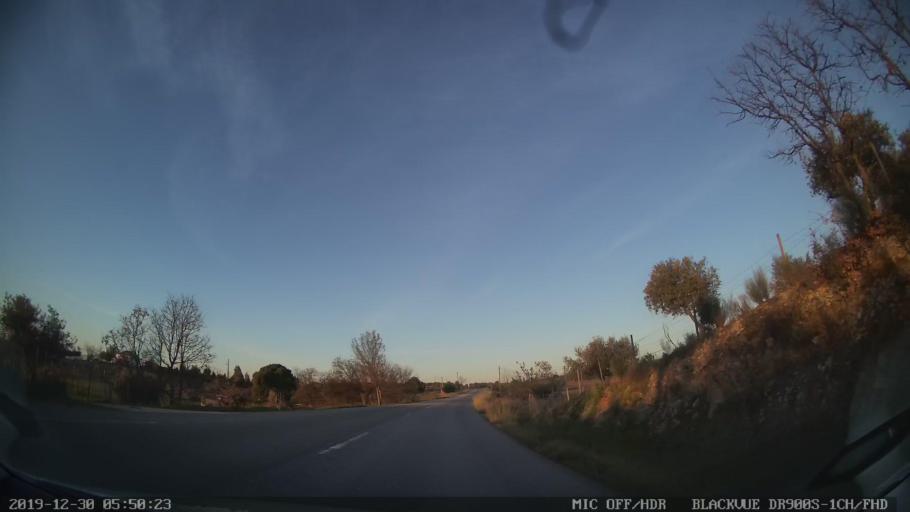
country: PT
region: Castelo Branco
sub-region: Idanha-A-Nova
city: Idanha-a-Nova
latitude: 39.9836
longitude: -7.2426
